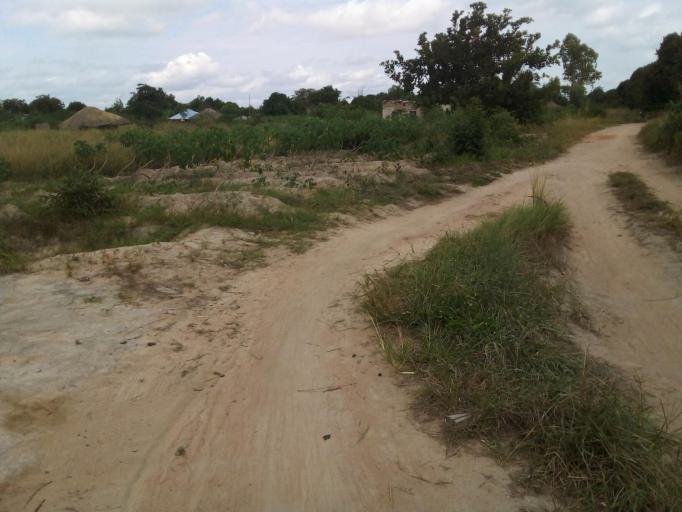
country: MZ
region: Zambezia
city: Quelimane
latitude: -17.5526
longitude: 36.7028
